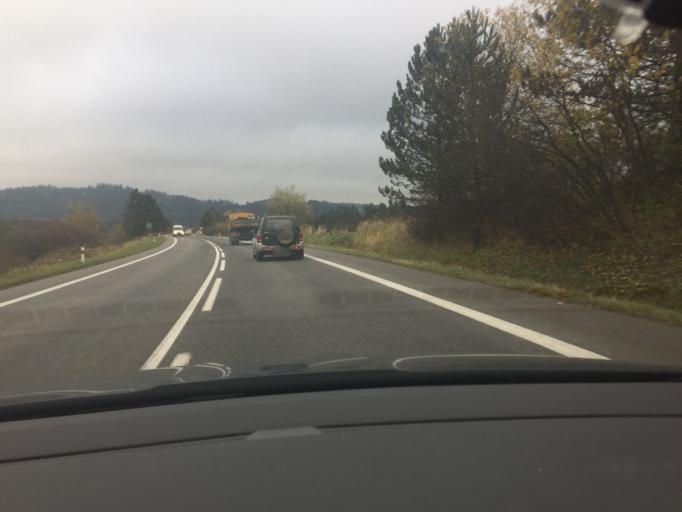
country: SK
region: Presovsky
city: Stara L'ubovna
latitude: 49.2856
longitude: 20.7342
